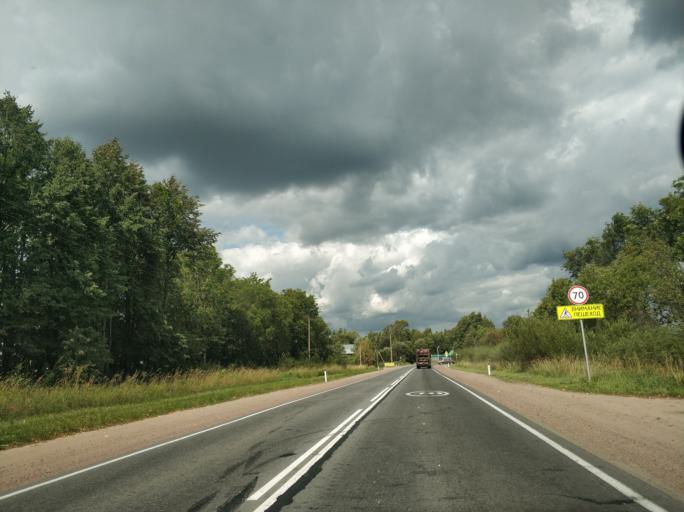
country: RU
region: Leningrad
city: Romanovka
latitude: 60.0659
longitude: 30.7413
